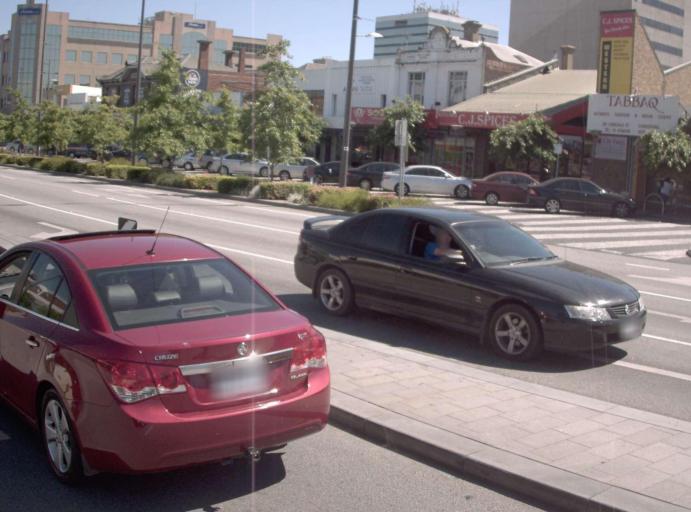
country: AU
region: Victoria
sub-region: Greater Dandenong
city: Dandenong
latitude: -37.9849
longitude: 145.2142
